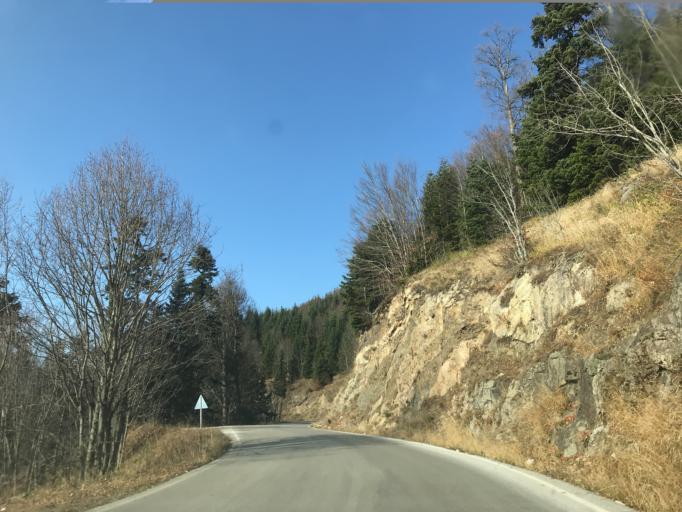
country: TR
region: Bolu
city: Bolu
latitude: 40.8857
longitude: 31.6824
